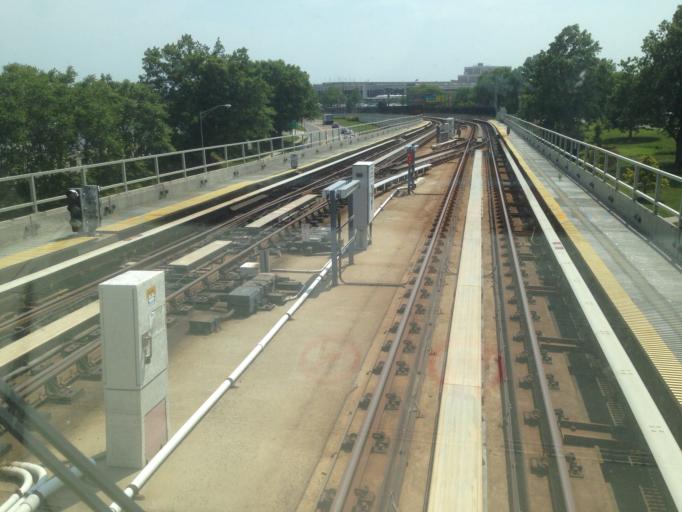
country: US
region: New York
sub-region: Queens County
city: Jamaica
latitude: 40.6575
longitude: -73.8059
